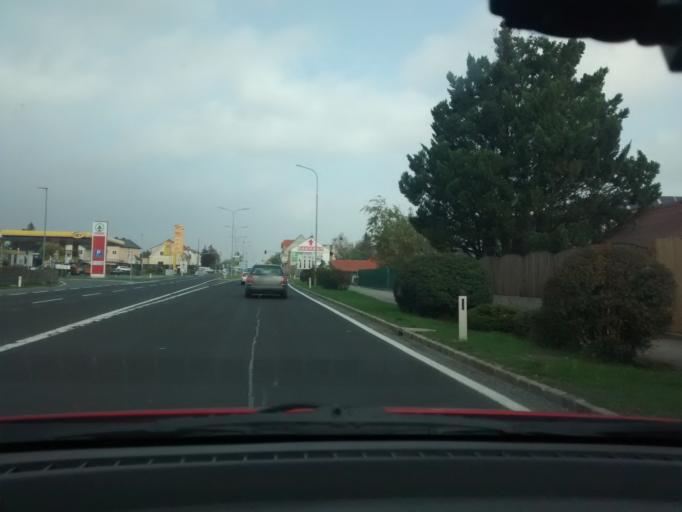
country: AT
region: Lower Austria
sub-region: Politischer Bezirk Modling
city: Guntramsdorf
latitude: 48.0461
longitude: 16.3063
